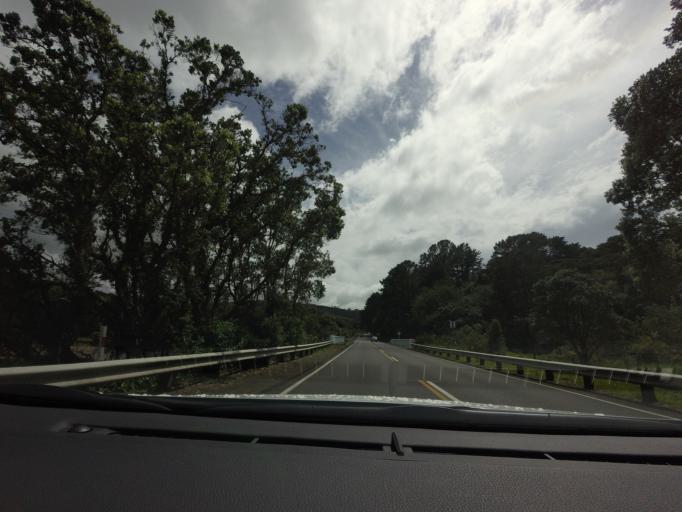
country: NZ
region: Auckland
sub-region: Auckland
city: Warkworth
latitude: -36.5618
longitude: 174.6963
